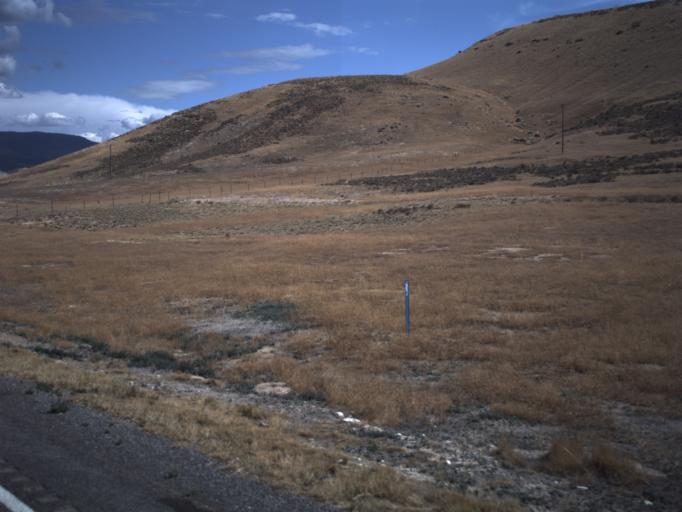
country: US
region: Utah
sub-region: Sanpete County
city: Gunnison
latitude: 39.1563
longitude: -111.7750
